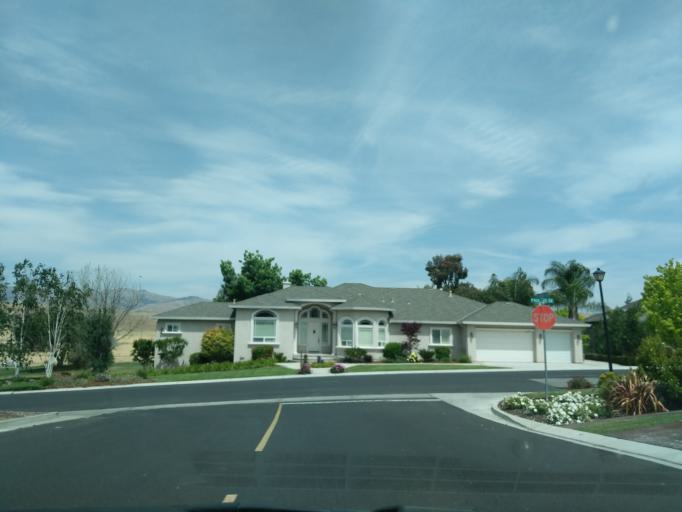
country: US
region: California
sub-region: San Benito County
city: Ridgemark
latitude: 36.8099
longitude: -121.3497
